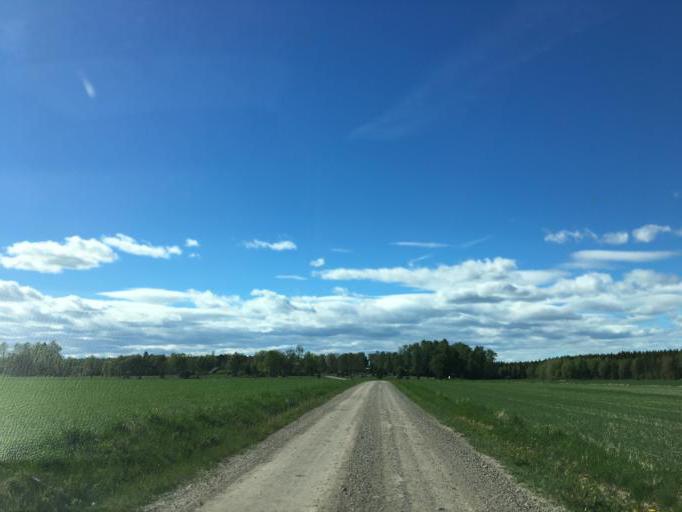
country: SE
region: Soedermanland
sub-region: Eskilstuna Kommun
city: Kvicksund
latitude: 59.3787
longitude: 16.2587
